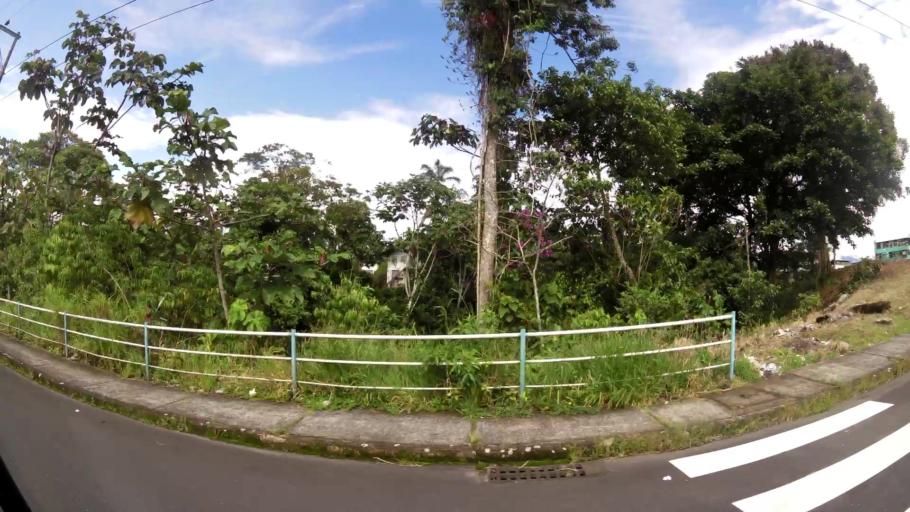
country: EC
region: Pastaza
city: Puyo
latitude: -1.5006
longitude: -78.0641
